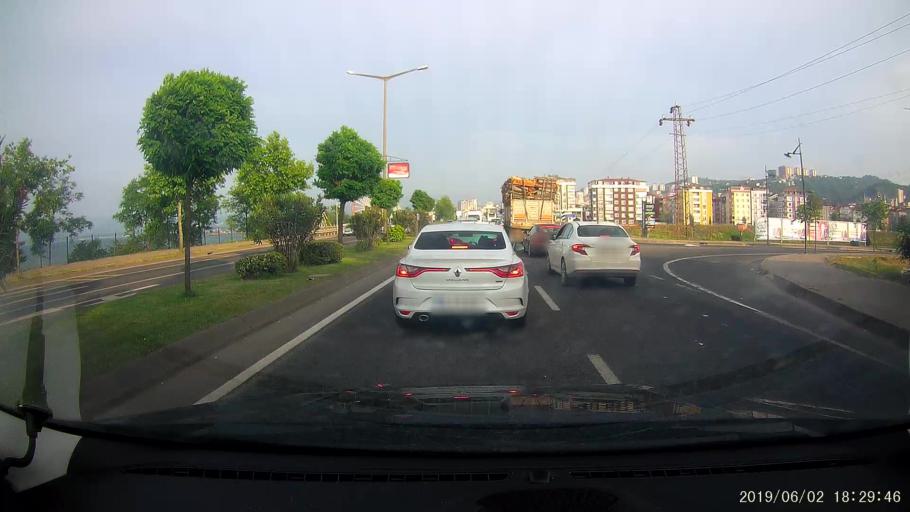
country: TR
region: Ordu
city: Fatsa
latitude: 41.0382
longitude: 37.4912
